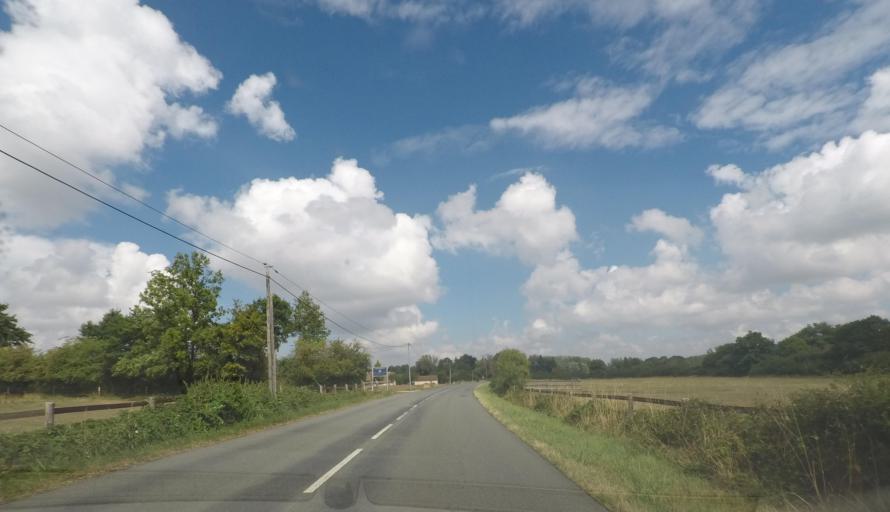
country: FR
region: Pays de la Loire
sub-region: Departement de la Sarthe
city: La Ferte-Bernard
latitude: 48.2666
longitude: 0.6001
